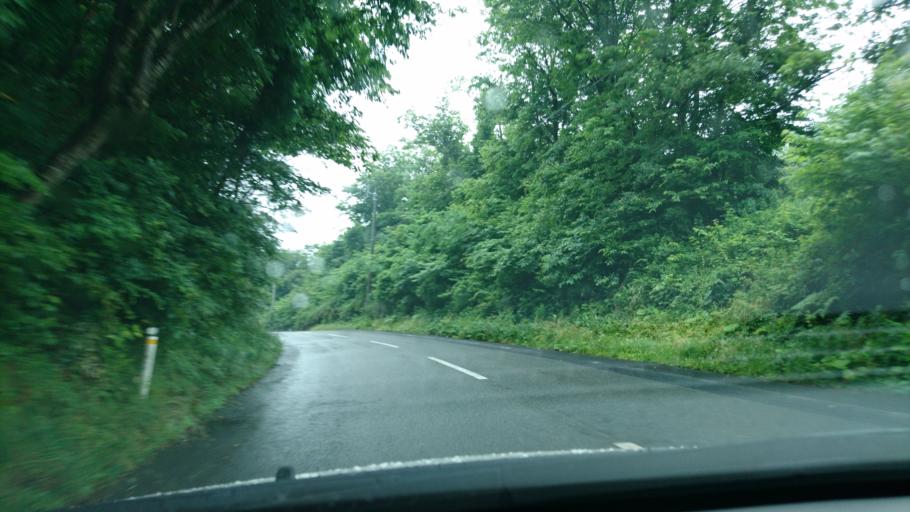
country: JP
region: Iwate
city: Ichinoseki
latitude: 38.9178
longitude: 141.0264
